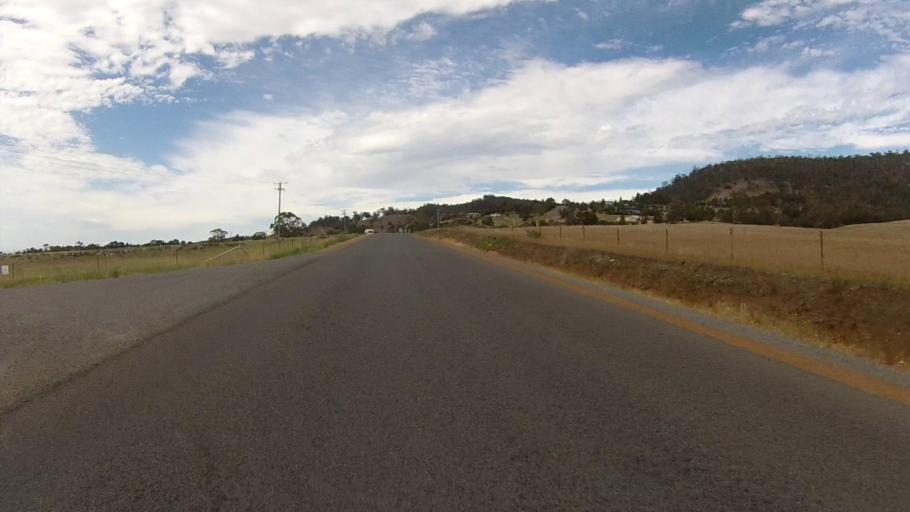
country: AU
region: Tasmania
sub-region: Brighton
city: Old Beach
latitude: -42.7379
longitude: 147.3529
